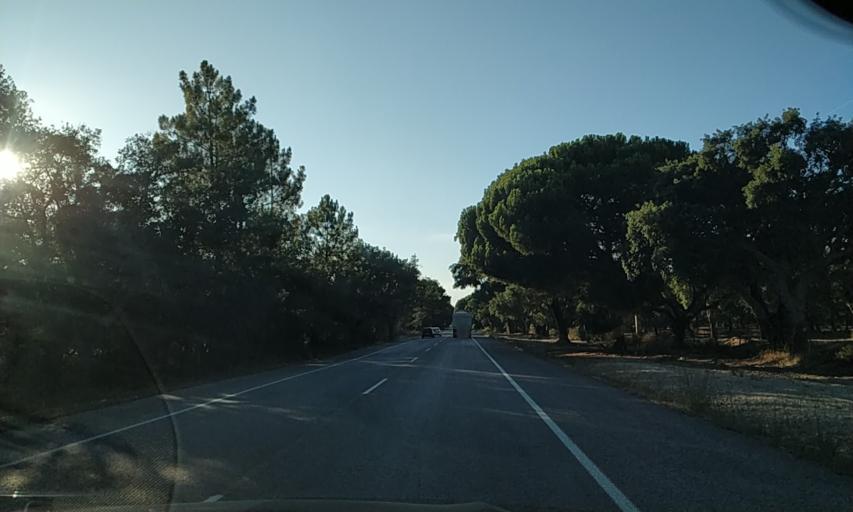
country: PT
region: Setubal
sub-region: Alcacer do Sal
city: Alcacer do Sal
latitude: 38.5308
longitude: -8.6282
